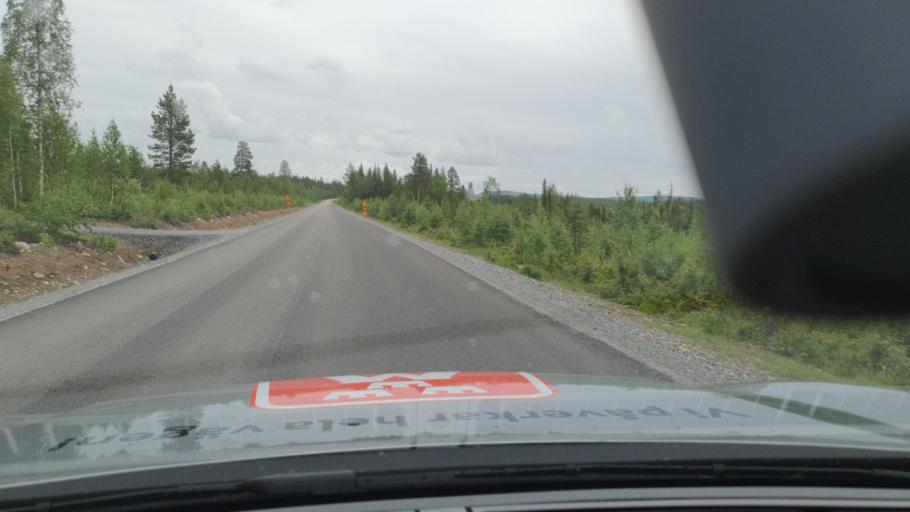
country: SE
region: Norrbotten
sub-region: Overtornea Kommun
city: OEvertornea
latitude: 66.5895
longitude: 23.3183
